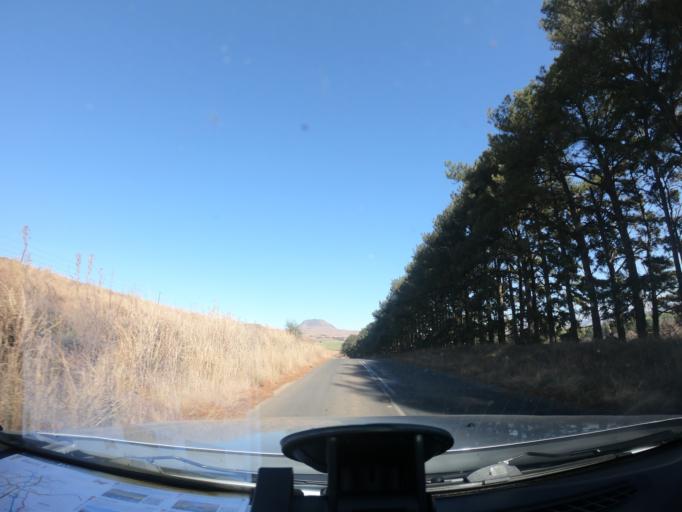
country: ZA
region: KwaZulu-Natal
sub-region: uMgungundlovu District Municipality
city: Mooirivier
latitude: -29.3303
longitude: 29.8217
